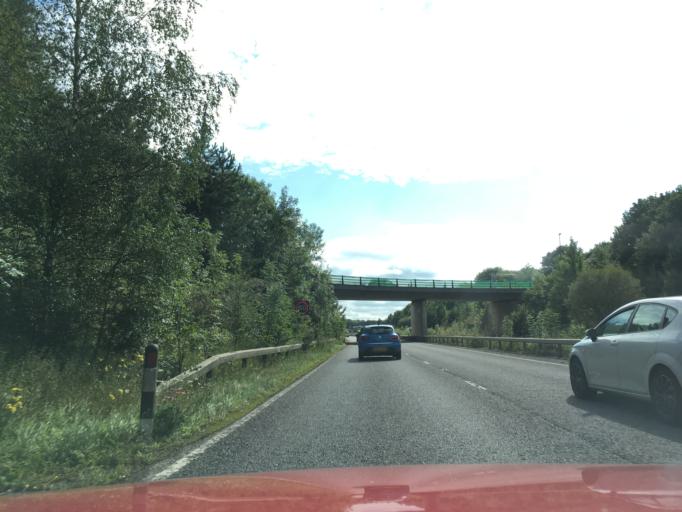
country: GB
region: England
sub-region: West Sussex
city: Horsham
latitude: 51.0692
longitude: -0.3523
